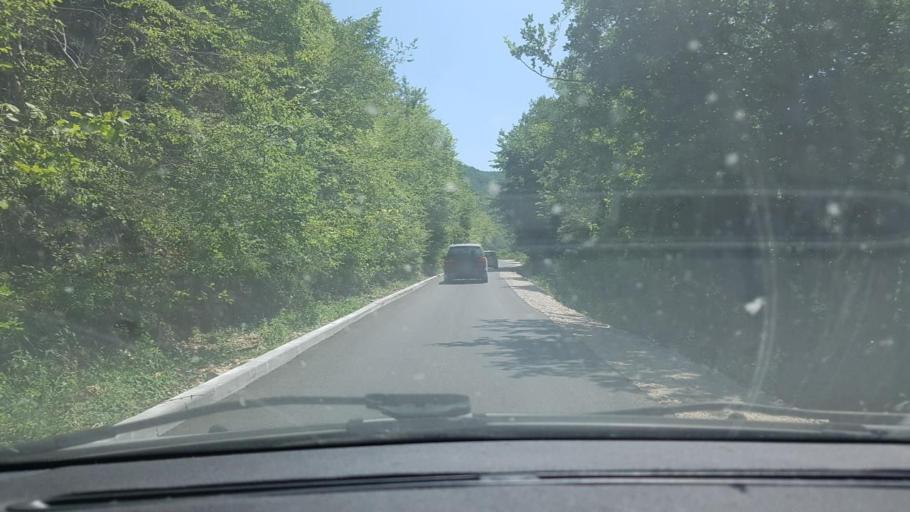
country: BA
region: Federation of Bosnia and Herzegovina
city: Orasac
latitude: 44.6247
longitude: 16.0557
